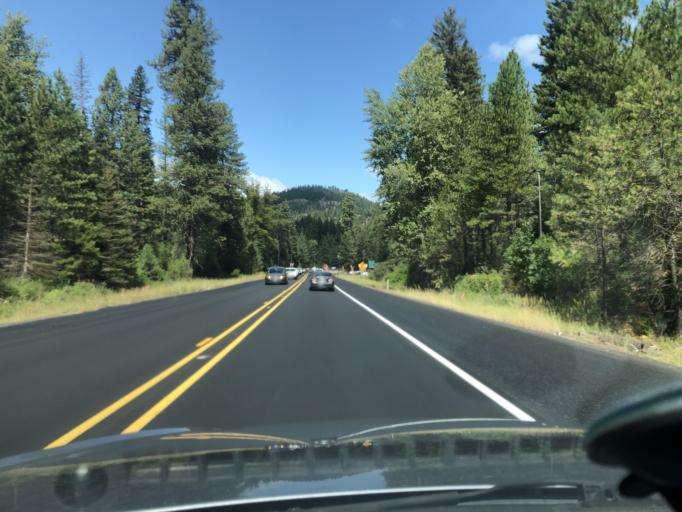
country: US
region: Washington
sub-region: Kittitas County
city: Cle Elum
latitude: 47.2889
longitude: -120.6979
